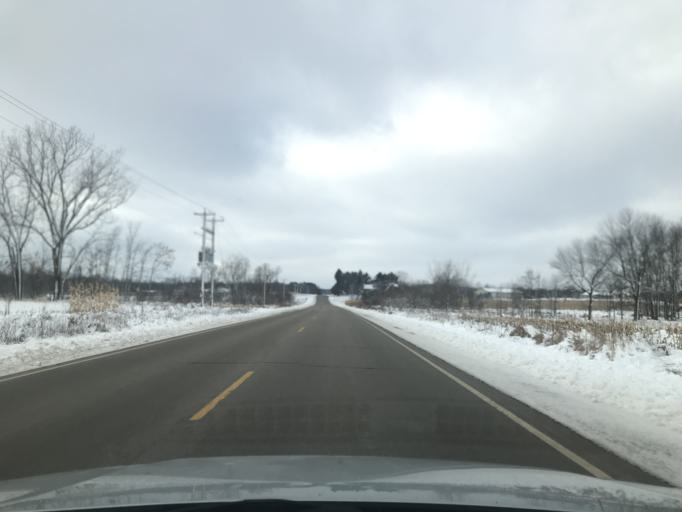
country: US
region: Wisconsin
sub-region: Oconto County
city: Oconto
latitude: 44.9503
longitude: -87.9665
